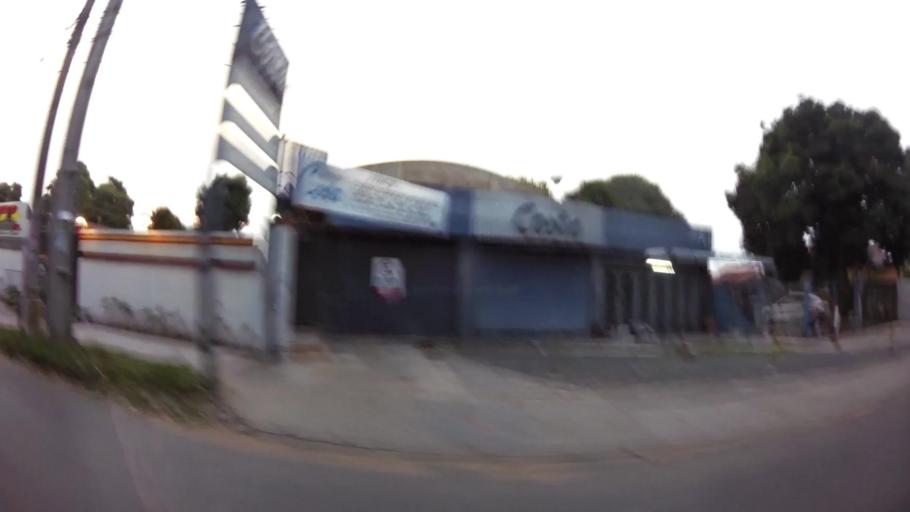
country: PY
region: Central
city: Lambare
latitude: -25.3285
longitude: -57.6185
